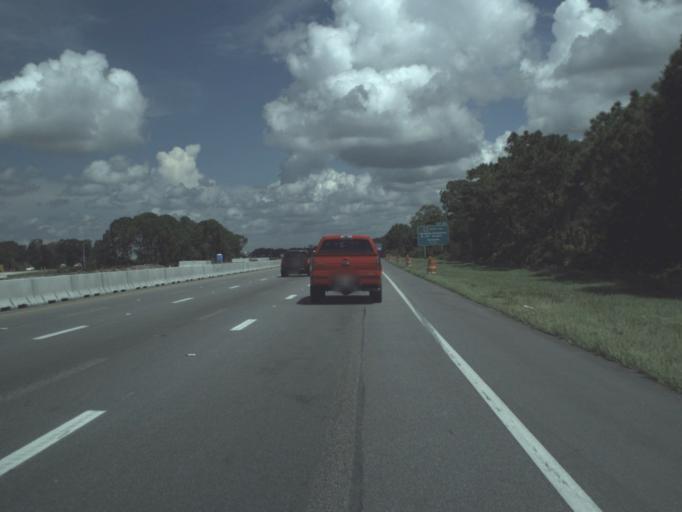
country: US
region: Florida
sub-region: Sarasota County
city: The Meadows
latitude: 27.3718
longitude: -82.4457
